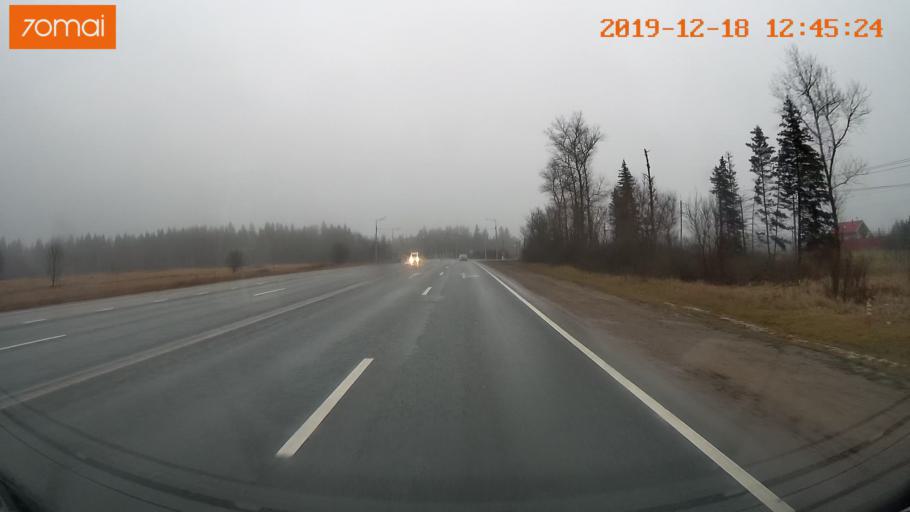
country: RU
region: Moskovskaya
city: Klin
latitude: 56.2309
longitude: 36.6589
